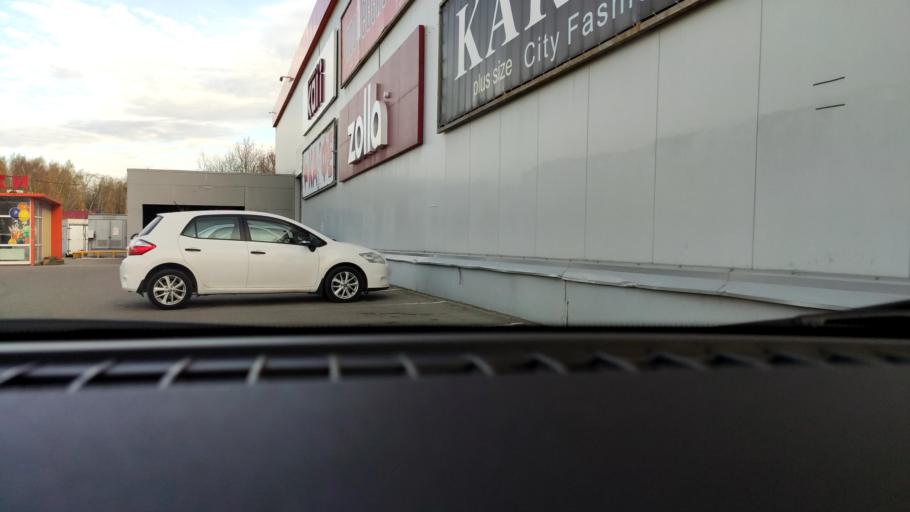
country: RU
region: Perm
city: Kondratovo
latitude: 58.0393
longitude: 56.0267
